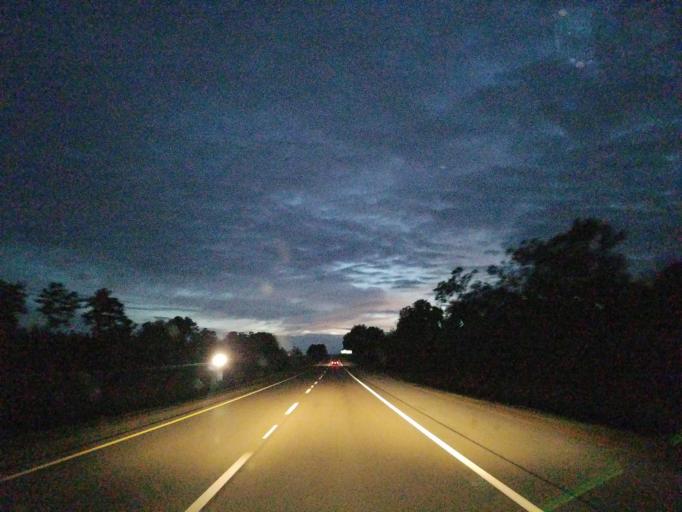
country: US
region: Mississippi
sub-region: Jones County
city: Sharon
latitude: 31.7399
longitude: -89.0875
